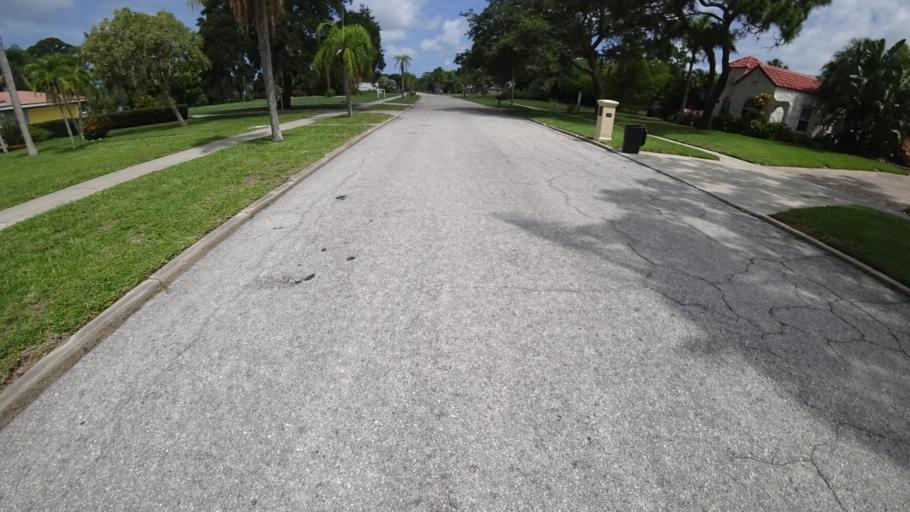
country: US
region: Florida
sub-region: Manatee County
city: Whitfield
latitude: 27.4070
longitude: -82.5735
